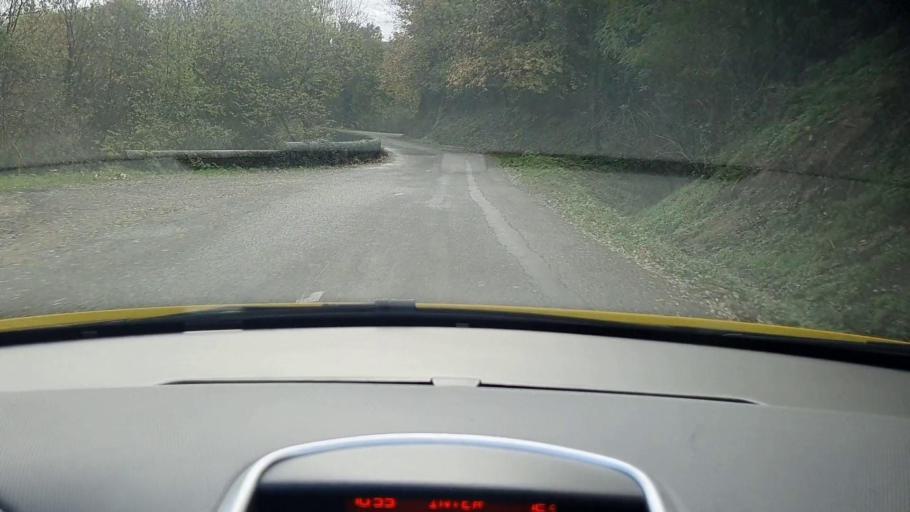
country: FR
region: Languedoc-Roussillon
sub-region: Departement du Gard
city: Lasalle
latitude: 44.0235
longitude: 3.8549
